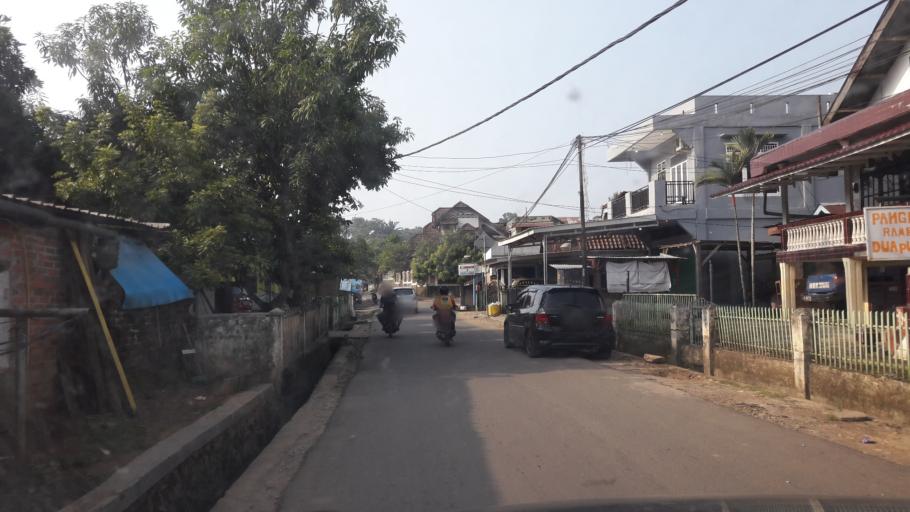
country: ID
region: South Sumatra
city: Gunungmegang Dalam
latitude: -3.2735
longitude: 103.8251
